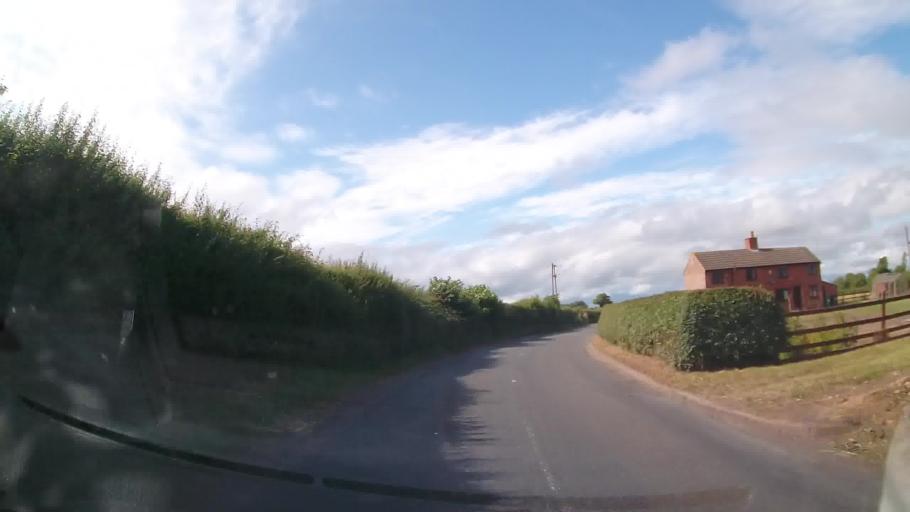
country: GB
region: England
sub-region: Shropshire
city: Petton
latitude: 52.8334
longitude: -2.8046
